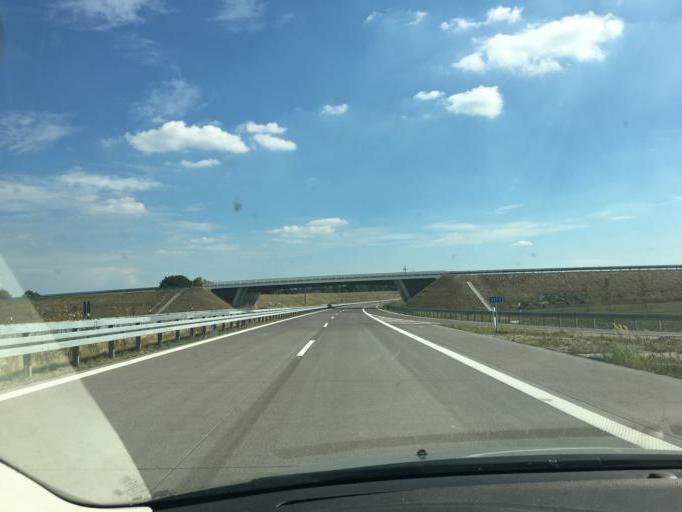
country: DE
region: Mecklenburg-Vorpommern
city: Grabow
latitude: 53.2233
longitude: 11.6139
